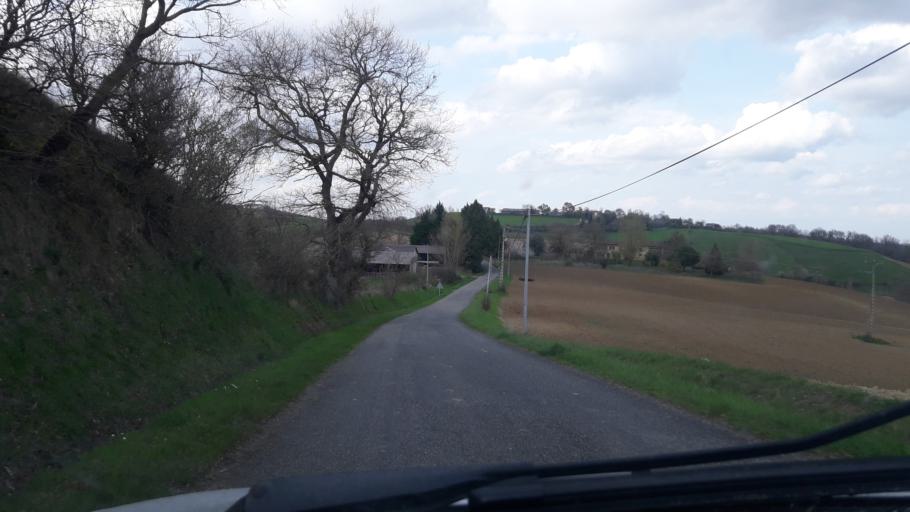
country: FR
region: Midi-Pyrenees
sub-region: Departement de la Haute-Garonne
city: Montesquieu-Volvestre
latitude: 43.2087
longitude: 1.3065
